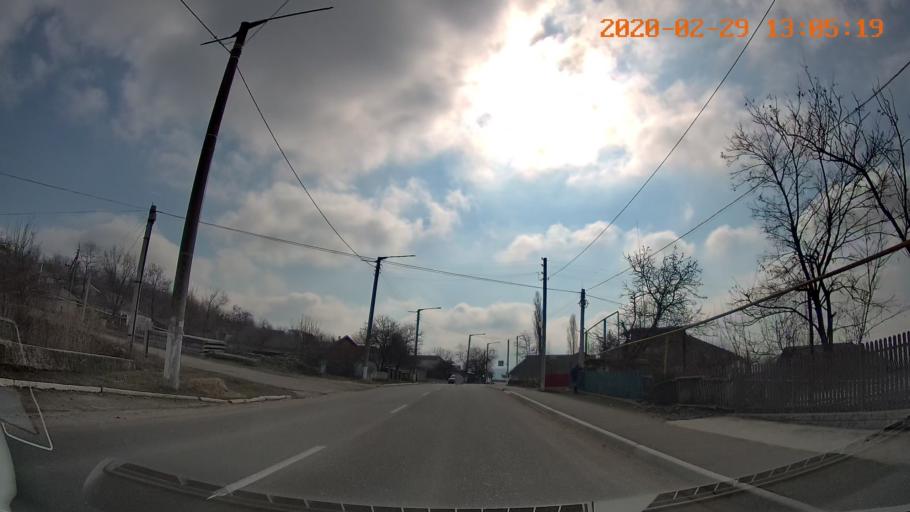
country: MD
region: Telenesti
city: Camenca
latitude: 48.0213
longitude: 28.7077
